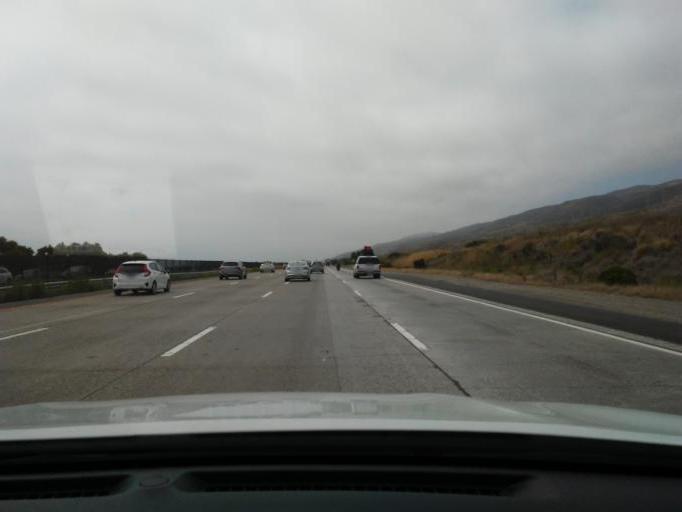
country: US
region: California
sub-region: Orange County
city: San Clemente
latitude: 33.3325
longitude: -117.4973
